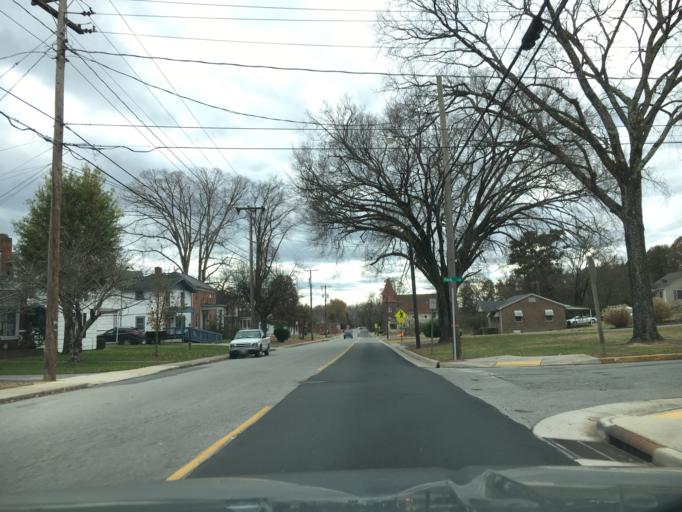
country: US
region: Virginia
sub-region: Halifax County
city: South Boston
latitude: 36.7136
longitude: -78.9015
